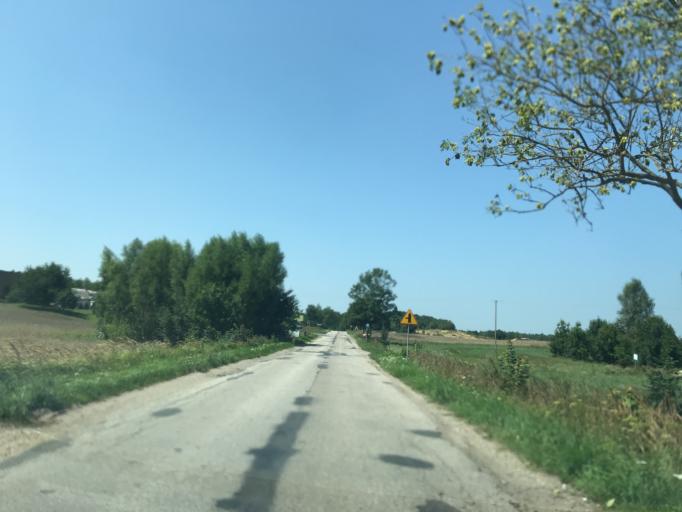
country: PL
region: Kujawsko-Pomorskie
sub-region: Powiat lipnowski
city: Chrostkowo
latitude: 52.9888
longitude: 19.2935
